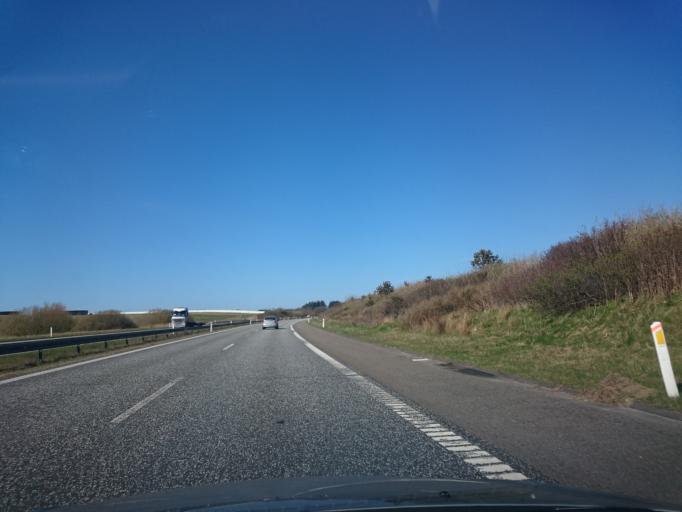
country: DK
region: North Denmark
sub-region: Hjorring Kommune
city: Hirtshals
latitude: 57.5443
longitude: 10.0062
